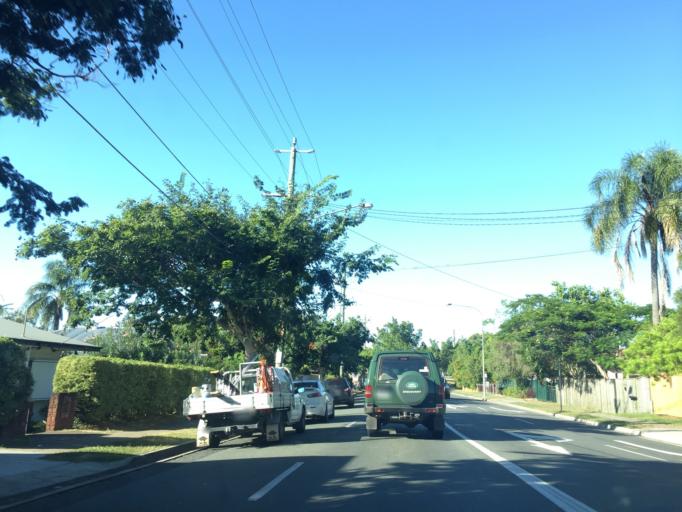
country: AU
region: Queensland
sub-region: Brisbane
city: Milton
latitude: -27.4493
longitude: 152.9774
